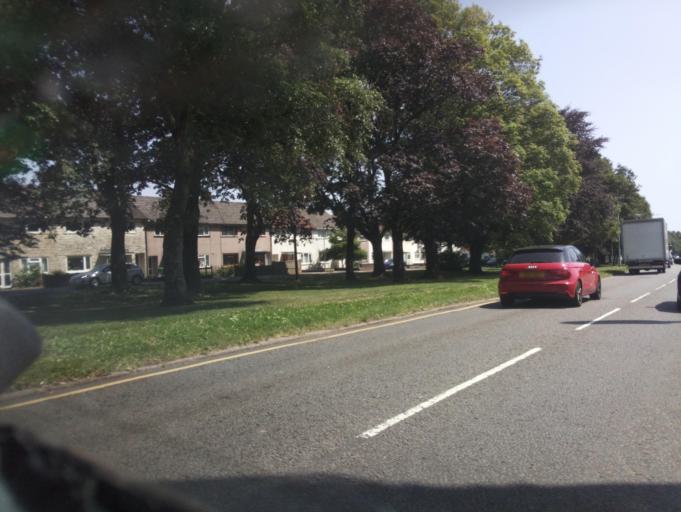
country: GB
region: Wales
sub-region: Caerphilly County Borough
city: Caerphilly
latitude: 51.5318
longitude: -3.2047
